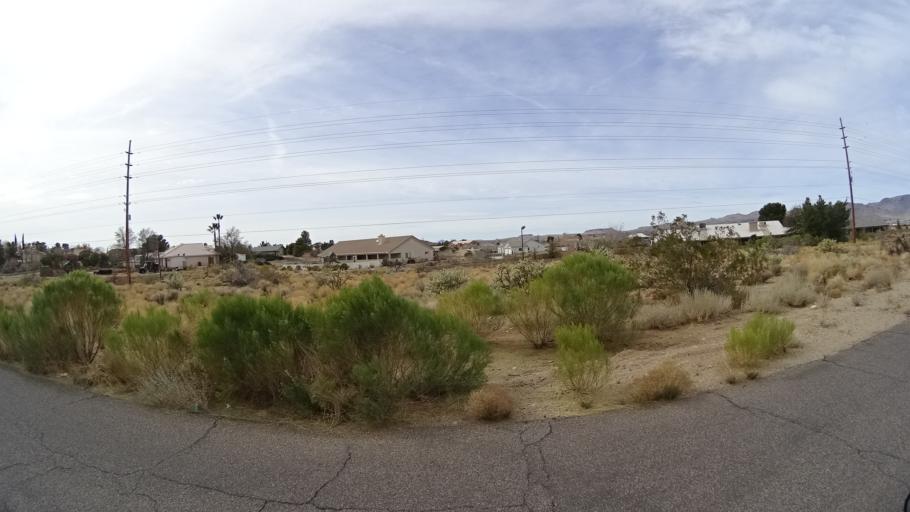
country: US
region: Arizona
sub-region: Mohave County
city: Kingman
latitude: 35.1952
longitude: -113.9864
